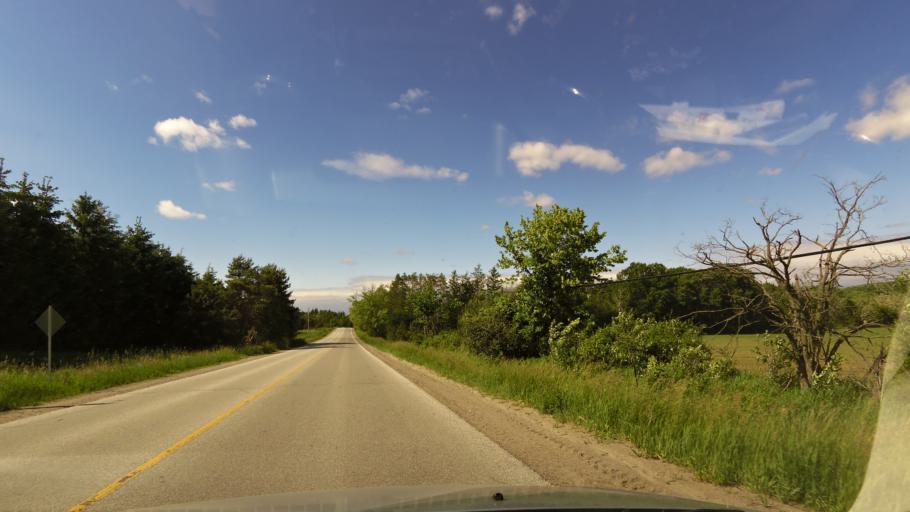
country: CA
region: Ontario
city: Bradford West Gwillimbury
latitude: 44.1815
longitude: -79.6204
